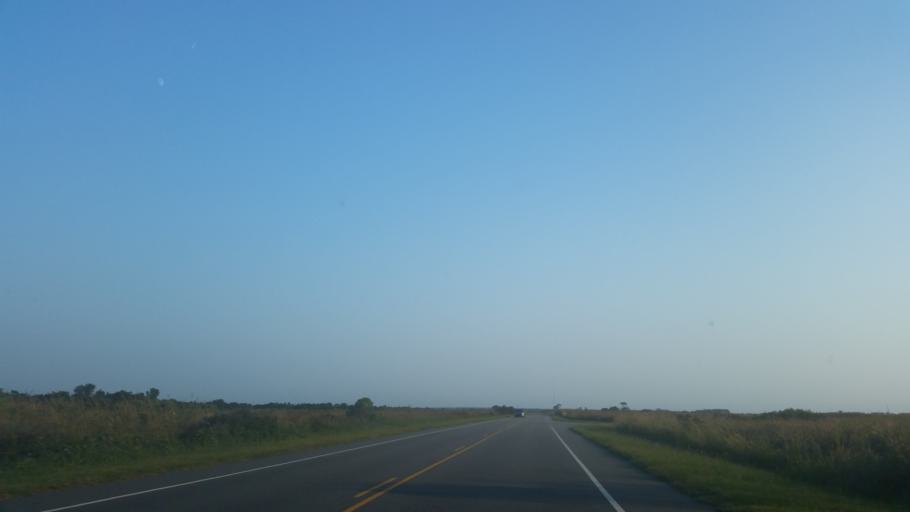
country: US
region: North Carolina
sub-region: Dare County
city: Wanchese
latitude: 35.8649
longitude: -75.5784
